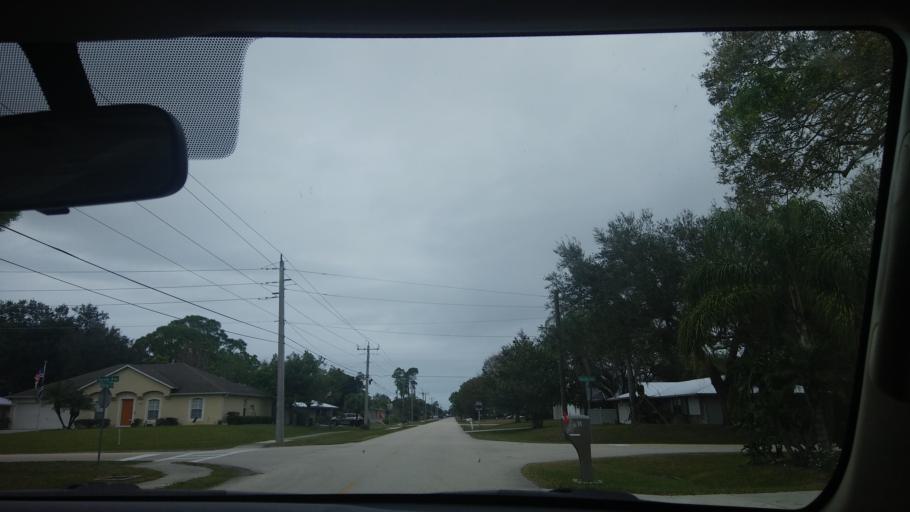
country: US
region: Florida
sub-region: Indian River County
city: Sebastian
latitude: 27.7924
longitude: -80.4948
